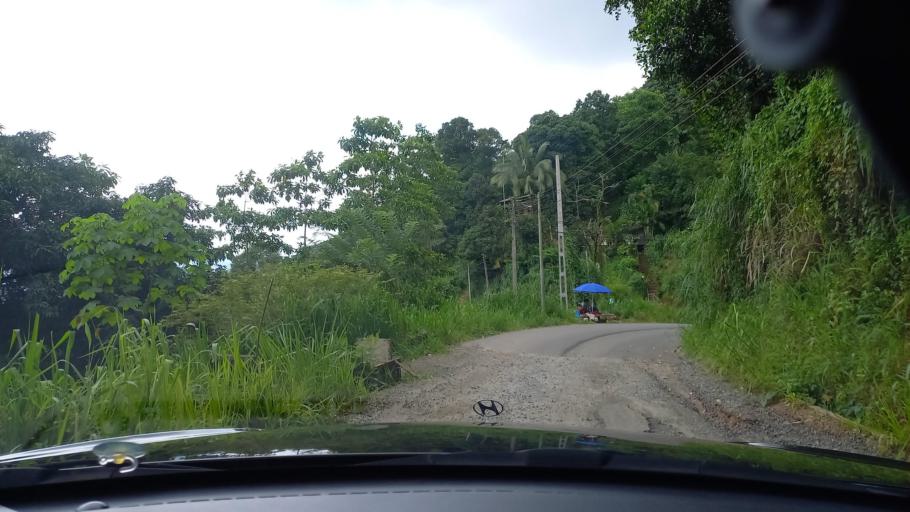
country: LK
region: Central
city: Gampola
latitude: 7.2096
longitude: 80.6210
